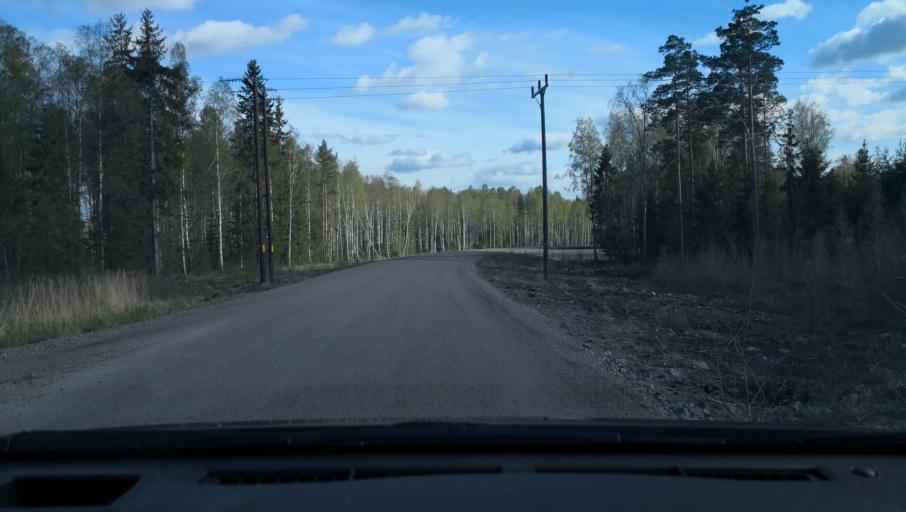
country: SE
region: OErebro
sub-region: Askersunds Kommun
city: Asbro
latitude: 58.9268
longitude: 15.0513
